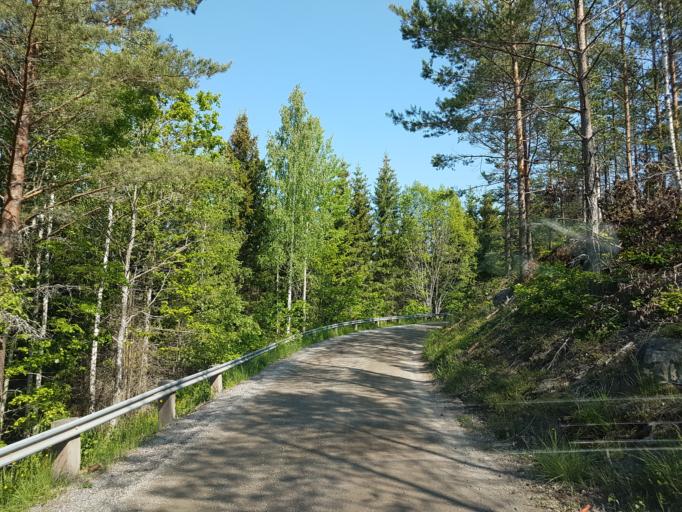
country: SE
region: OEstergoetland
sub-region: Atvidabergs Kommun
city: Atvidaberg
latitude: 58.1985
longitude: 16.1525
